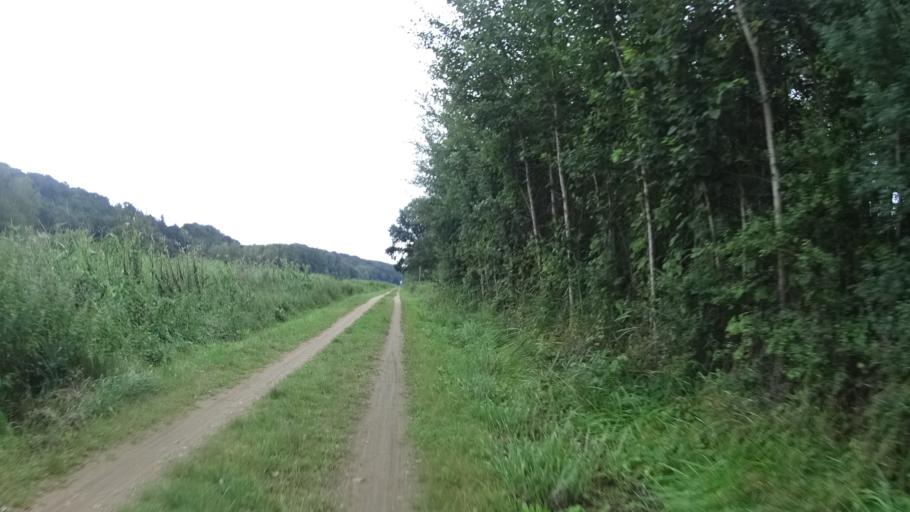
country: DE
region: Schleswig-Holstein
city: Alt Molln
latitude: 53.6419
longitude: 10.6546
